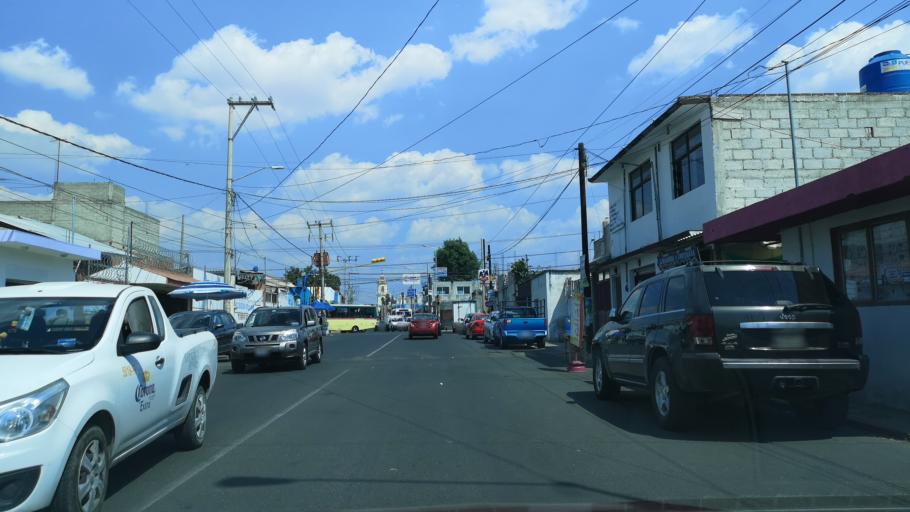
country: MX
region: Puebla
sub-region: Cuautlancingo
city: Sanctorum
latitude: 19.0871
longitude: -98.2146
